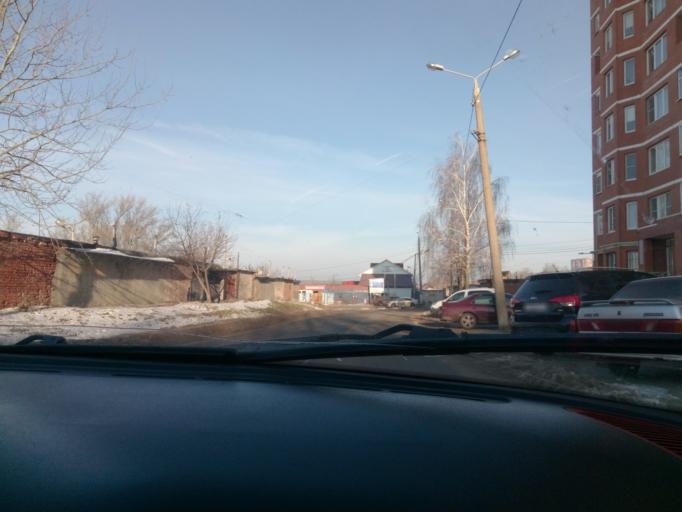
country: RU
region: Tula
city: Mendeleyevskiy
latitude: 54.1674
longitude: 37.5617
